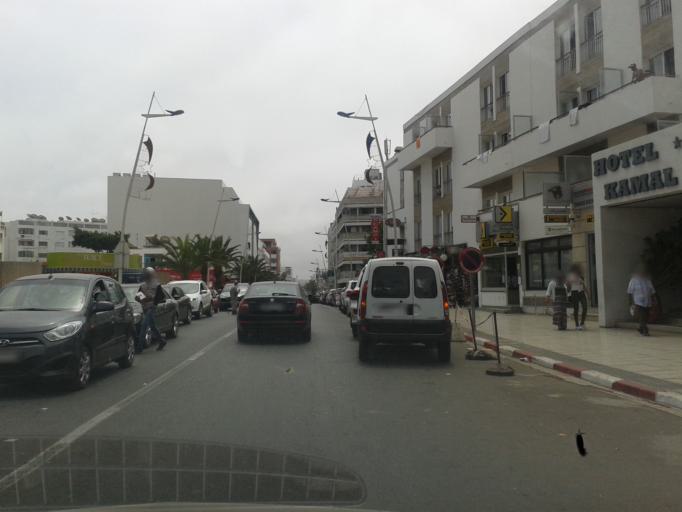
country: MA
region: Souss-Massa-Draa
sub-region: Agadir-Ida-ou-Tnan
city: Agadir
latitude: 30.4197
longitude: -9.5987
